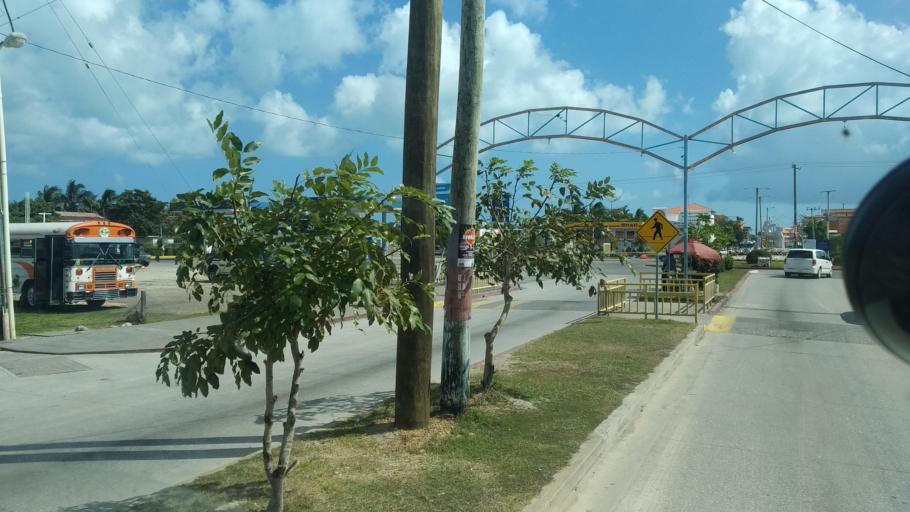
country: BZ
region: Belize
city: Belize City
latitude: 17.4964
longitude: -88.1990
